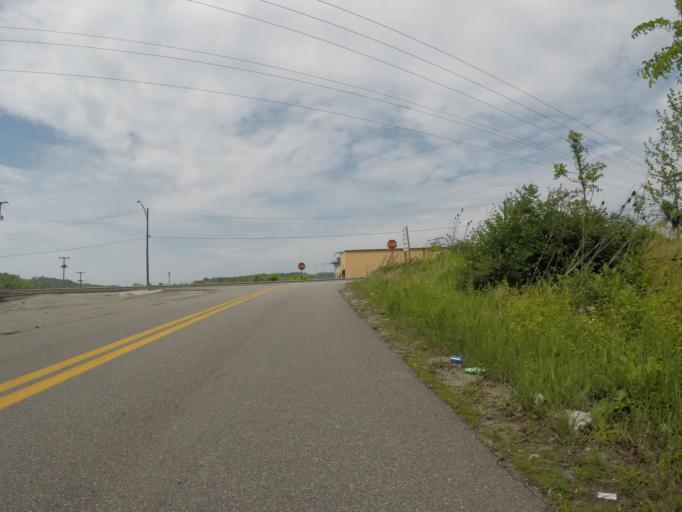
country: US
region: West Virginia
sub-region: Wayne County
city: Kenova
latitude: 38.3353
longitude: -82.5800
